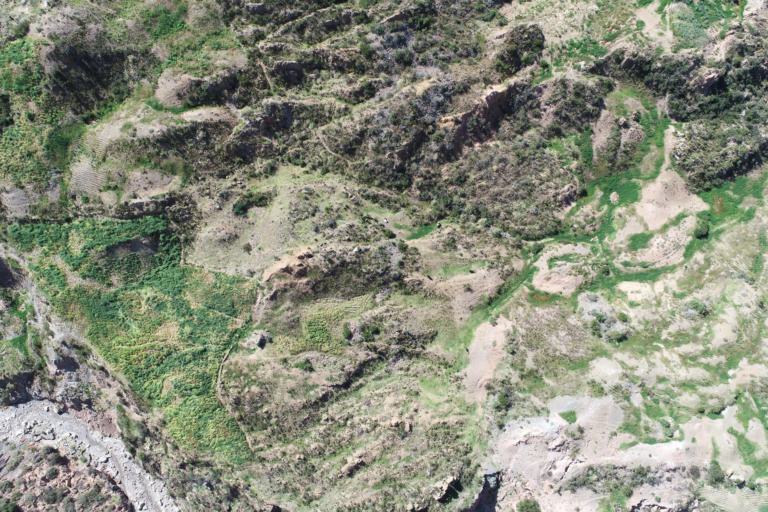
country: BO
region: La Paz
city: La Paz
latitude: -16.5592
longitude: -67.9883
